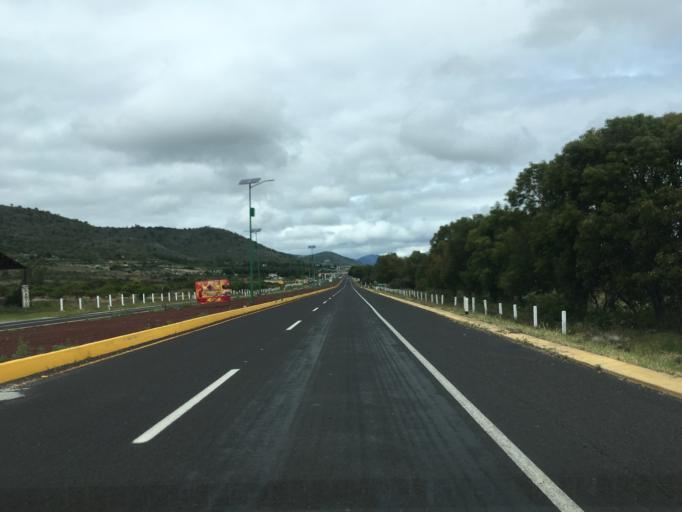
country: MX
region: Hidalgo
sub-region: Atotonilco el Grande
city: La Estancia
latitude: 20.3219
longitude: -98.6945
